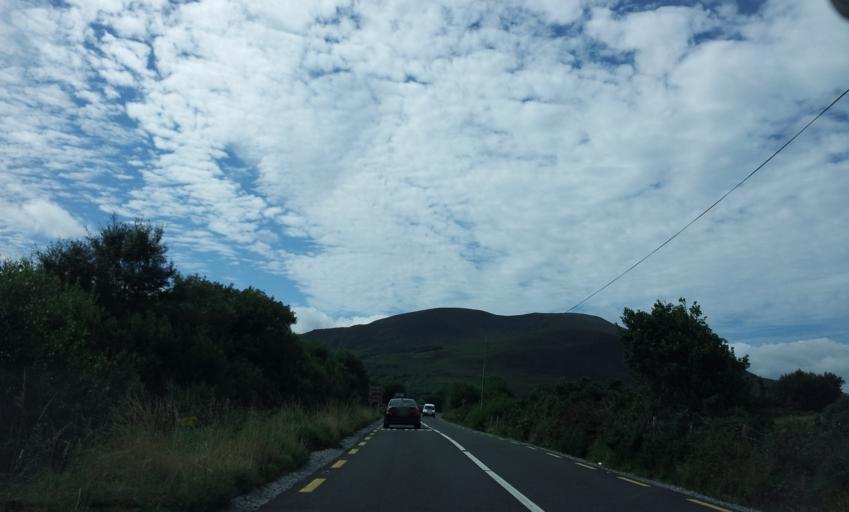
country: IE
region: Munster
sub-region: Ciarrai
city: Killorglin
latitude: 52.0730
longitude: -9.8822
